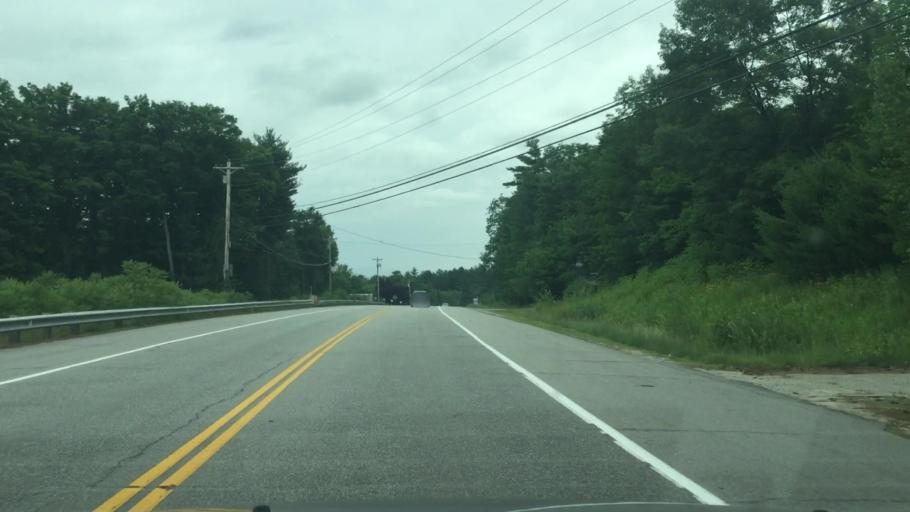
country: US
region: New Hampshire
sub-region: Carroll County
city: Moultonborough
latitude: 43.7658
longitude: -71.3852
